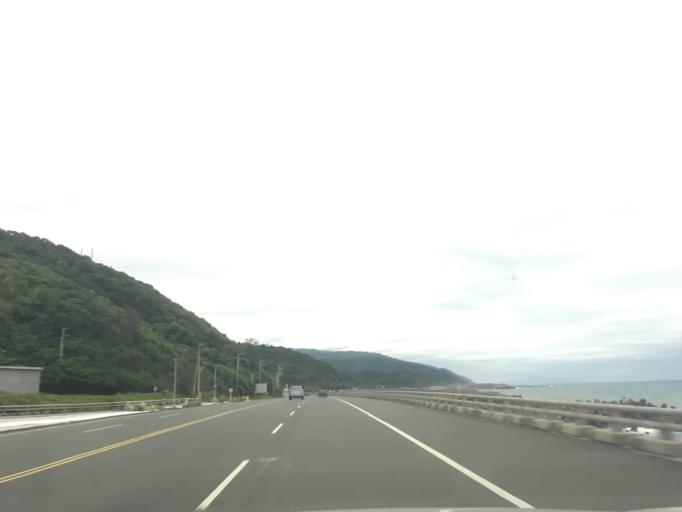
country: TW
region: Taiwan
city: Hengchun
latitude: 22.3234
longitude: 120.8919
